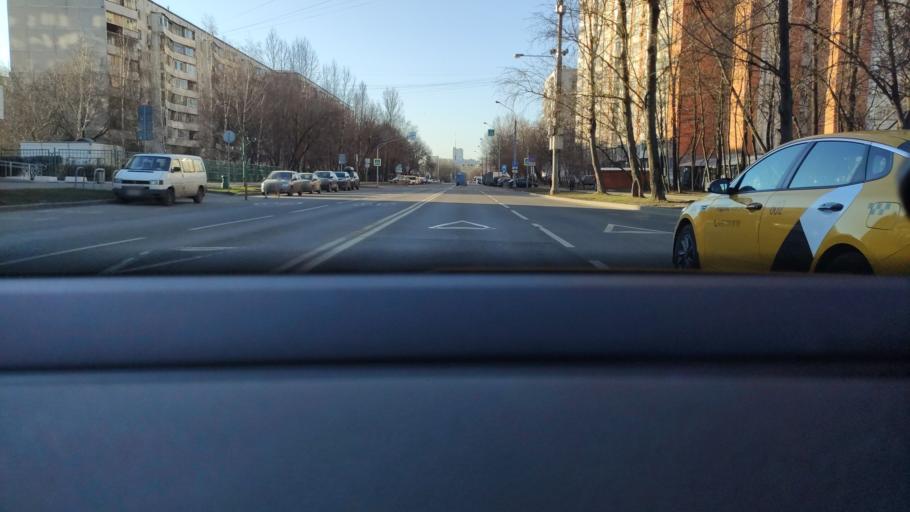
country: RU
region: Moscow
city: Leonovo
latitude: 55.8747
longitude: 37.6458
